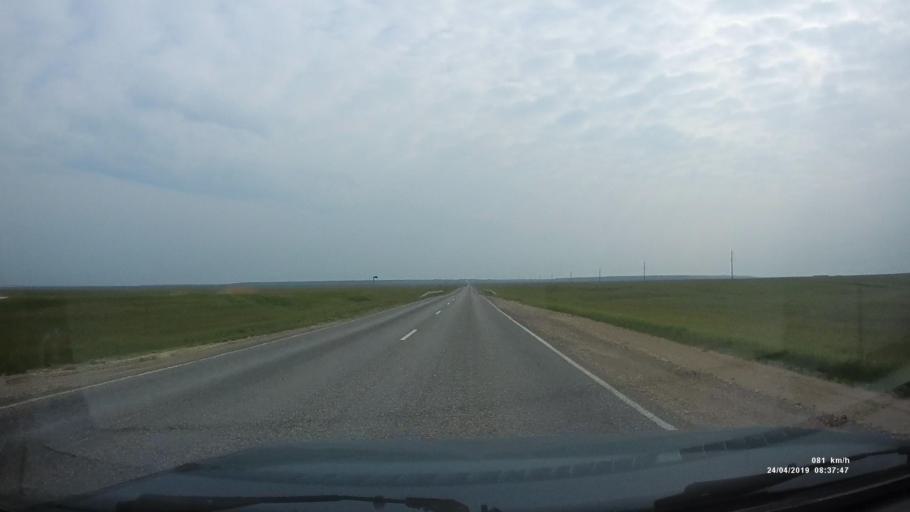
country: RU
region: Kalmykiya
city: Arshan'
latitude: 46.2119
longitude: 43.9566
